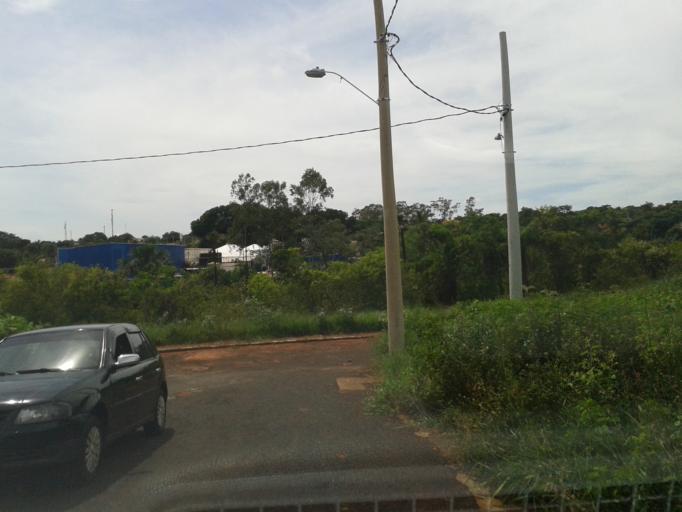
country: BR
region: Minas Gerais
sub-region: Santa Vitoria
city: Santa Vitoria
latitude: -18.8428
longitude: -50.1339
